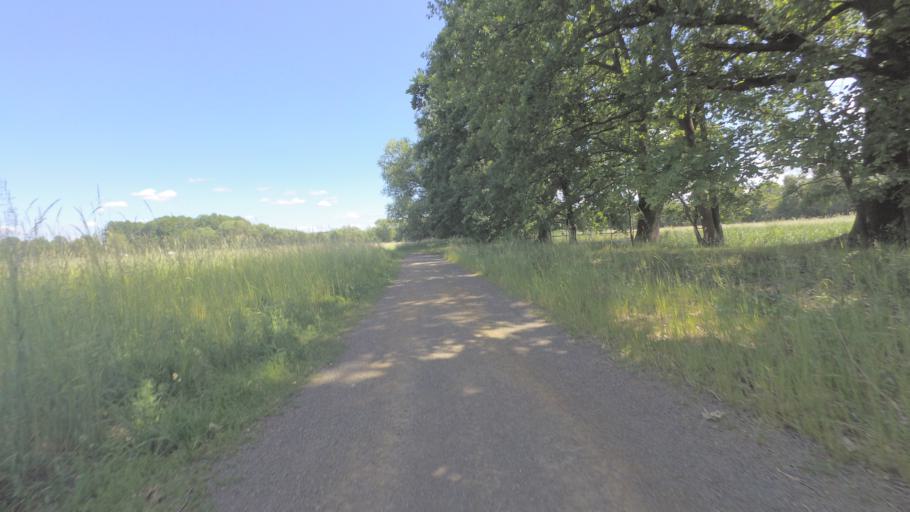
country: DE
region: Brandenburg
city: Rangsdorf
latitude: 52.3023
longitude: 13.4495
